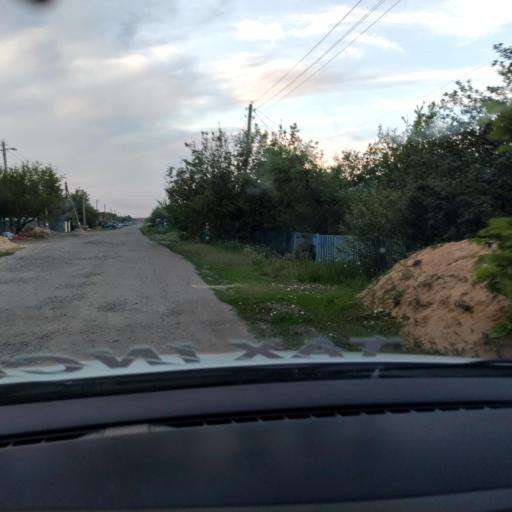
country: RU
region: Voronezj
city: Maslovka
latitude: 51.4492
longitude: 39.2364
